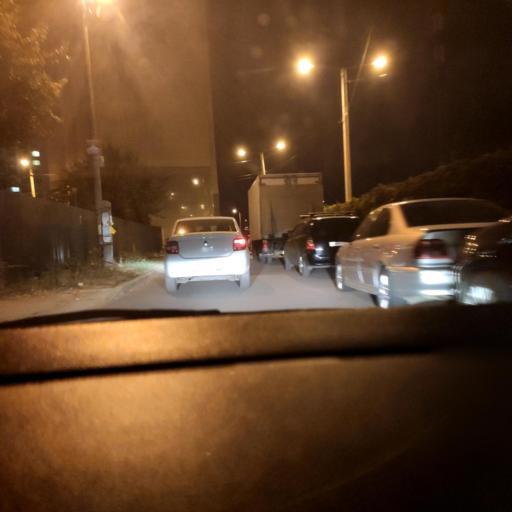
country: RU
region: Voronezj
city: Voronezh
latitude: 51.6750
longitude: 39.1332
